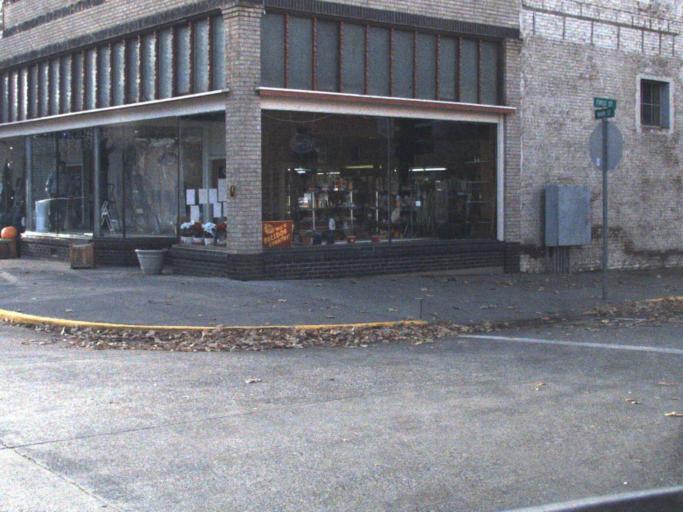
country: US
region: Washington
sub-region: Columbia County
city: Dayton
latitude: 46.3197
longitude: -117.9806
